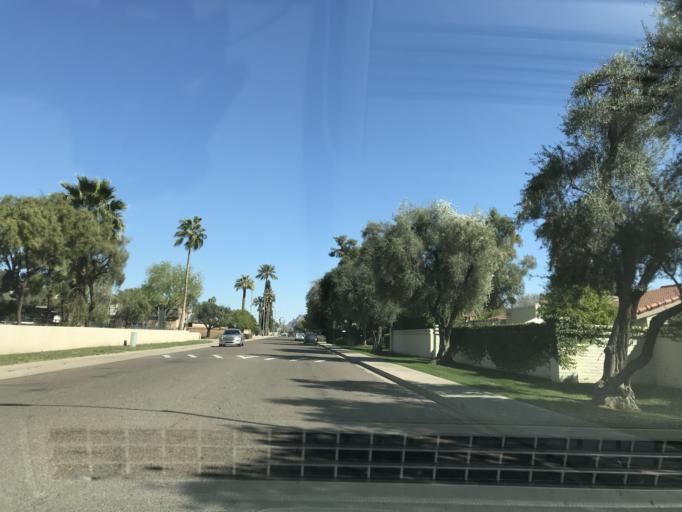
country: US
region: Arizona
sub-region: Maricopa County
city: Phoenix
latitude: 33.5201
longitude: -112.0704
